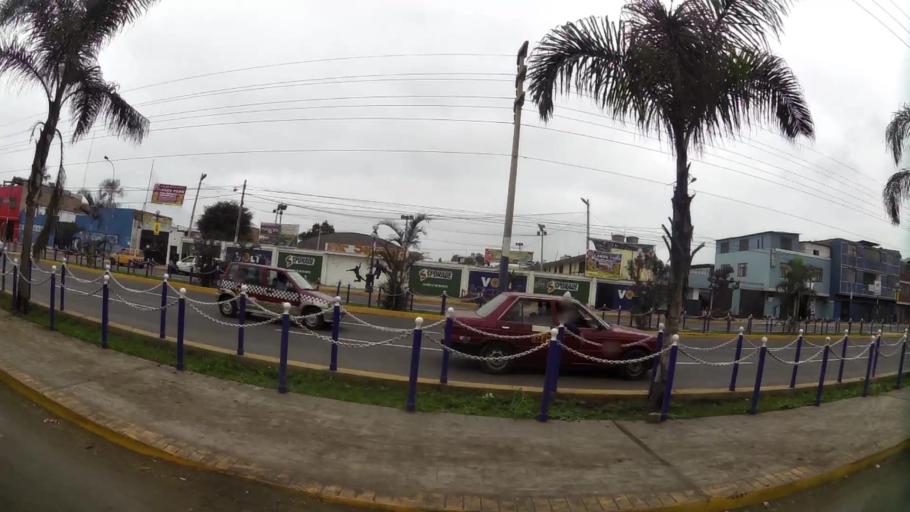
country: PE
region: Lima
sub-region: Lima
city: Surco
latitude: -12.1963
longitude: -77.0001
